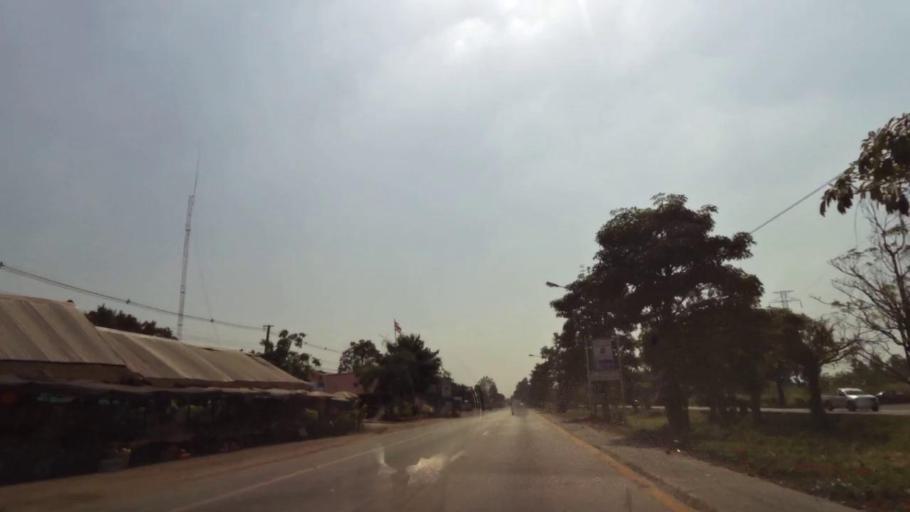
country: TH
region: Phichit
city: Wachira Barami
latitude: 16.5048
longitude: 100.1435
